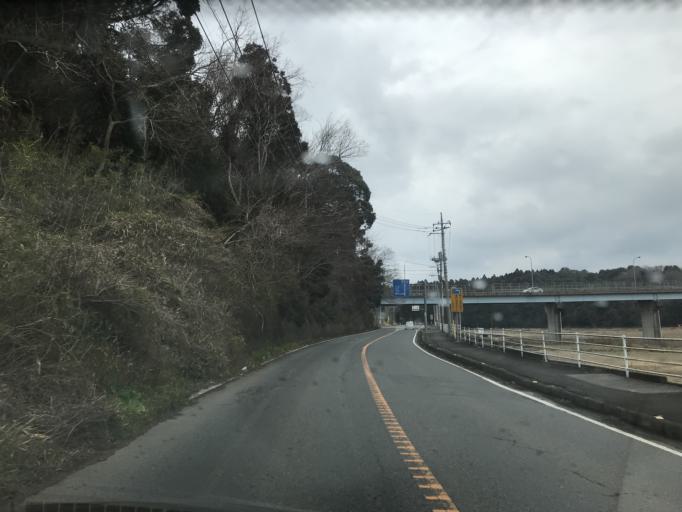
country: JP
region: Chiba
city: Sawara
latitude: 35.8270
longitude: 140.5039
